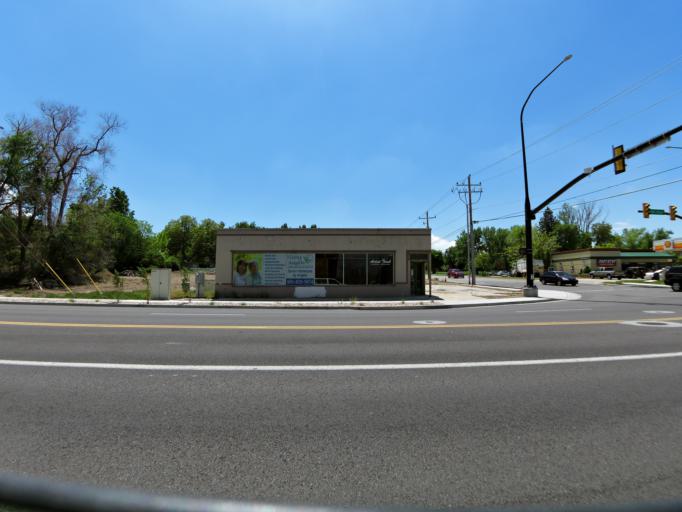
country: US
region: Utah
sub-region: Weber County
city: South Ogden
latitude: 41.1906
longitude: -111.9681
